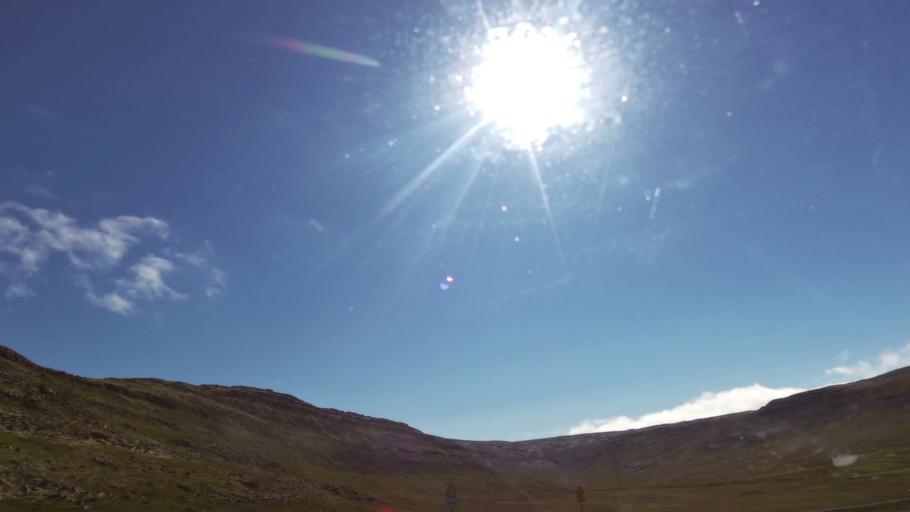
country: IS
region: West
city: Olafsvik
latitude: 65.5596
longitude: -24.1703
